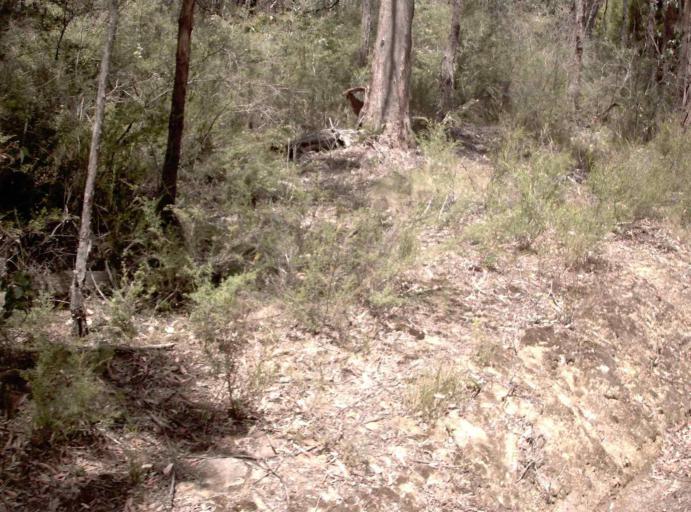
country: AU
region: Victoria
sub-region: East Gippsland
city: Lakes Entrance
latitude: -37.5872
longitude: 147.8926
